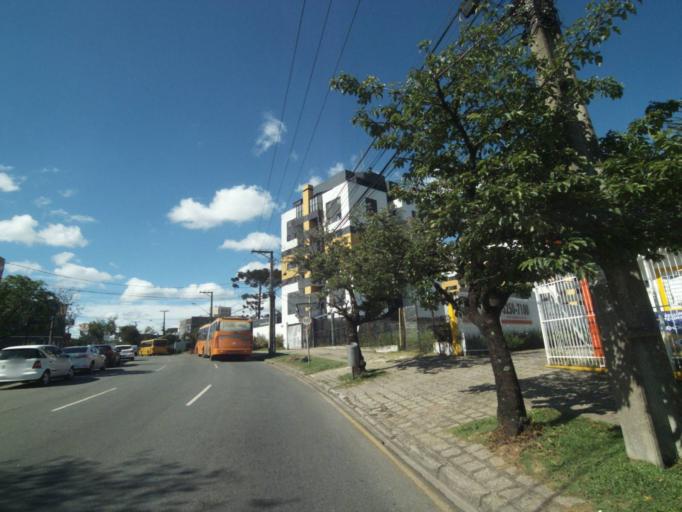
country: BR
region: Parana
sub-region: Curitiba
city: Curitiba
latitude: -25.3993
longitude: -49.2573
